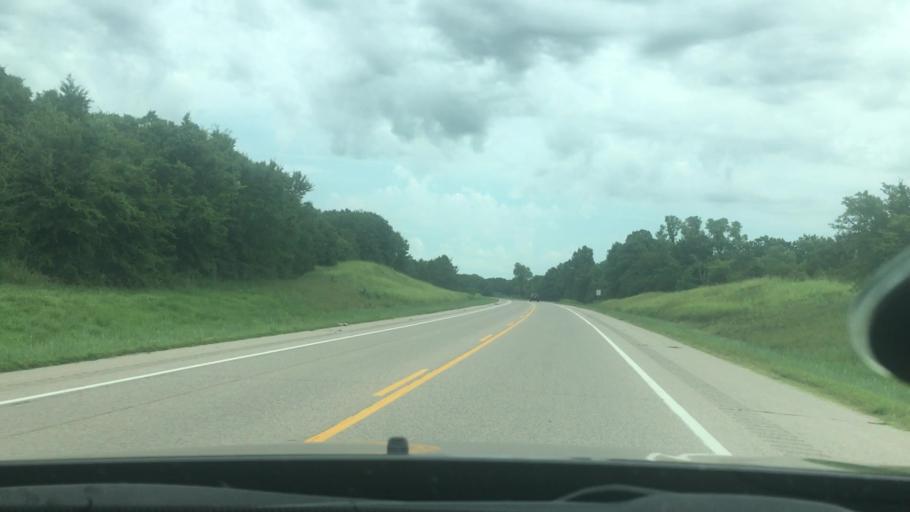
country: US
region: Oklahoma
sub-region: Seminole County
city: Konawa
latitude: 34.9504
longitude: -96.6797
